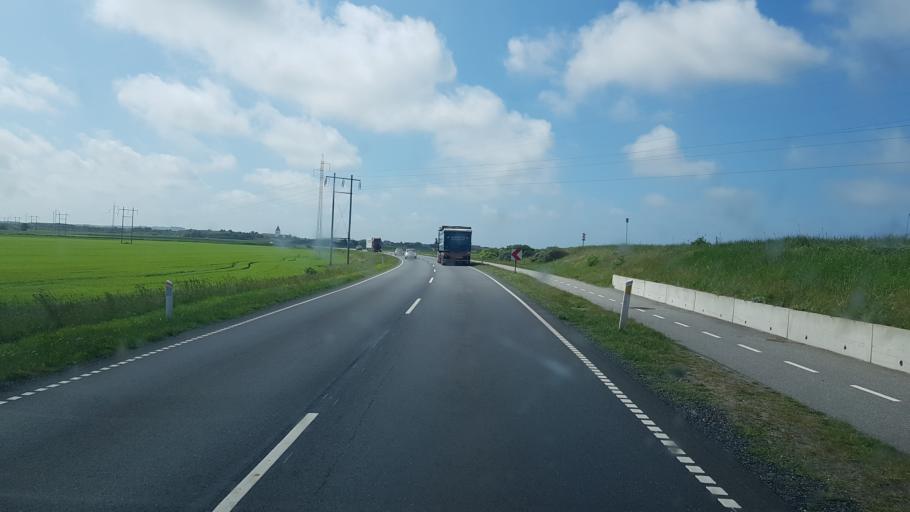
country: DK
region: Central Jutland
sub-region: Lemvig Kommune
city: Harboore
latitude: 56.6322
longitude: 8.1846
